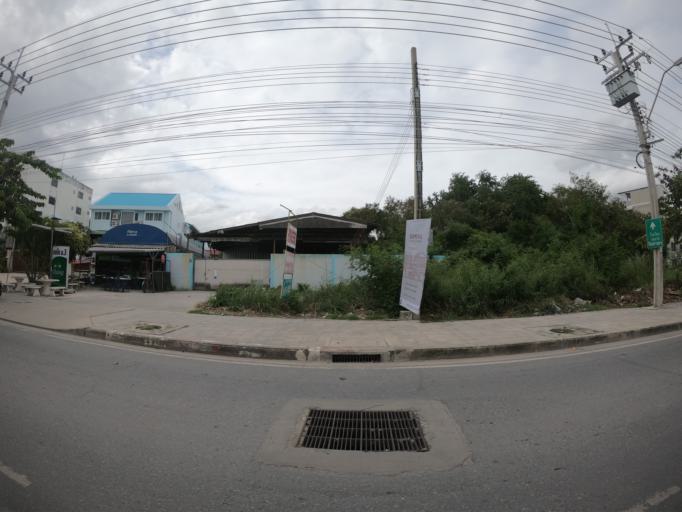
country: TH
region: Bangkok
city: Bang Na
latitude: 13.6820
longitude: 100.6720
